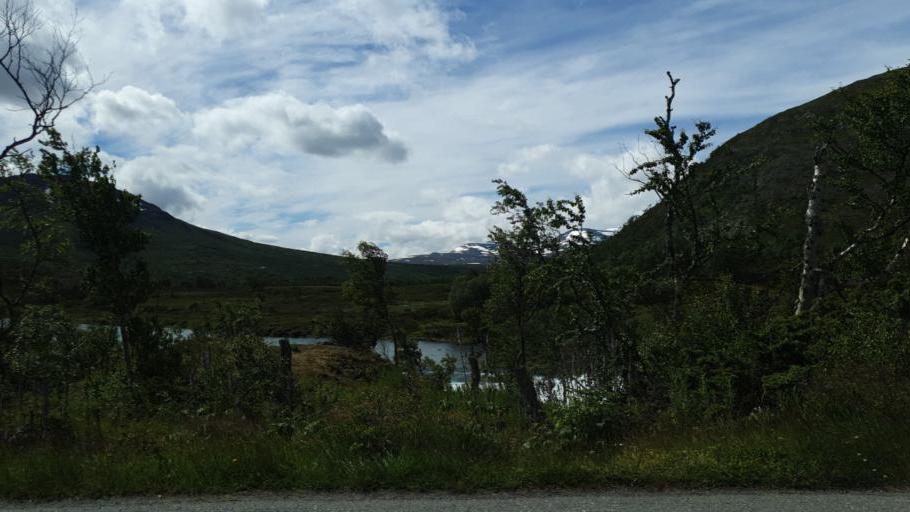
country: NO
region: Oppland
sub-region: Oystre Slidre
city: Heggenes
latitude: 61.4905
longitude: 8.8188
